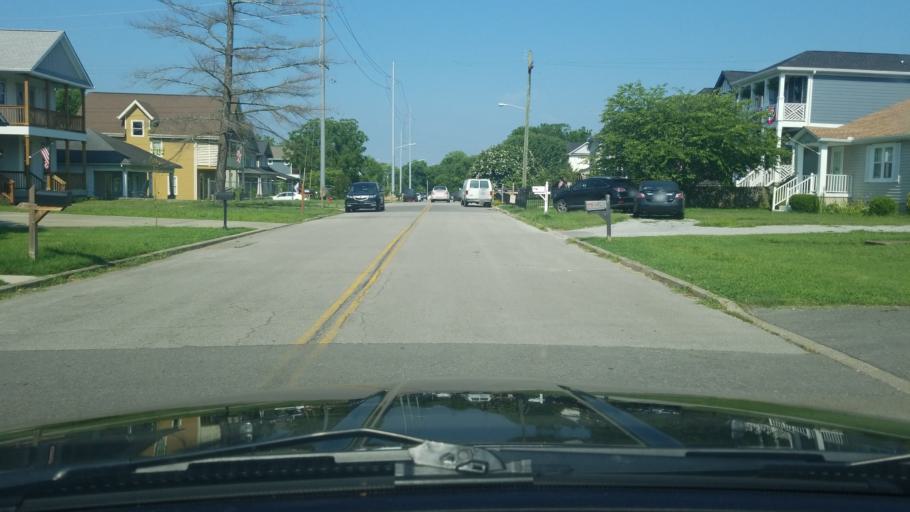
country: US
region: Tennessee
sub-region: Davidson County
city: Belle Meade
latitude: 36.1576
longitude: -86.8507
